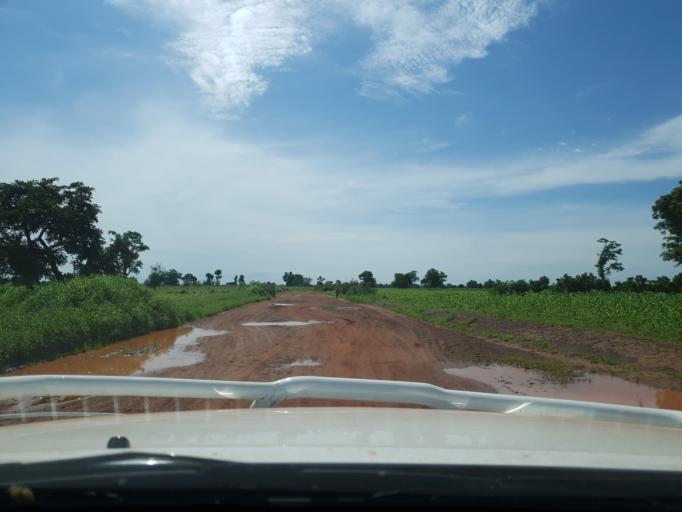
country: ML
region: Koulikoro
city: Banamba
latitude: 13.2806
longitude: -7.5530
